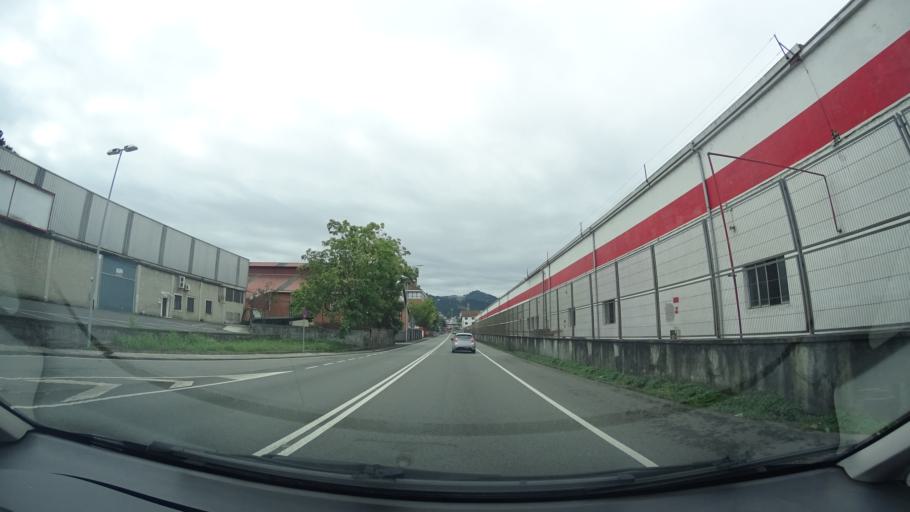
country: ES
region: Basque Country
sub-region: Bizkaia
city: Galdakao
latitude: 43.2213
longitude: -2.8160
